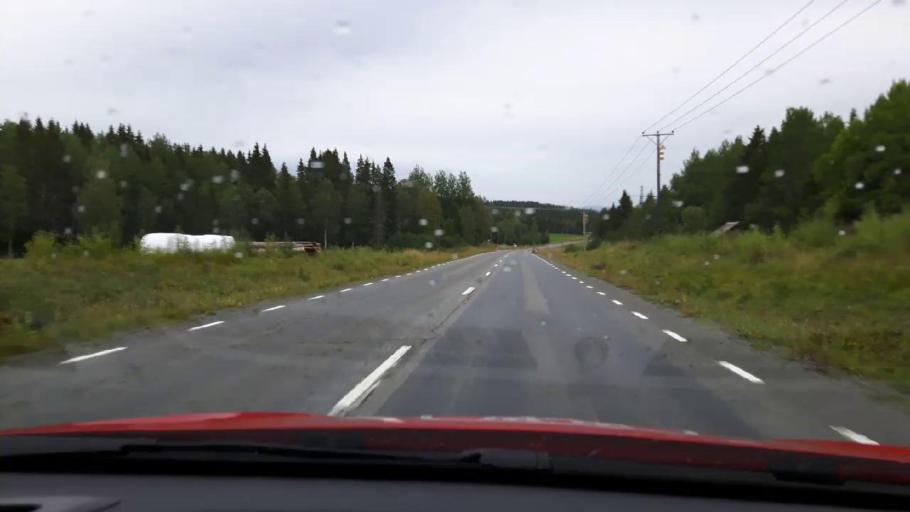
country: SE
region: Jaemtland
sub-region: Are Kommun
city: Jarpen
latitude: 63.3824
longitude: 13.4213
